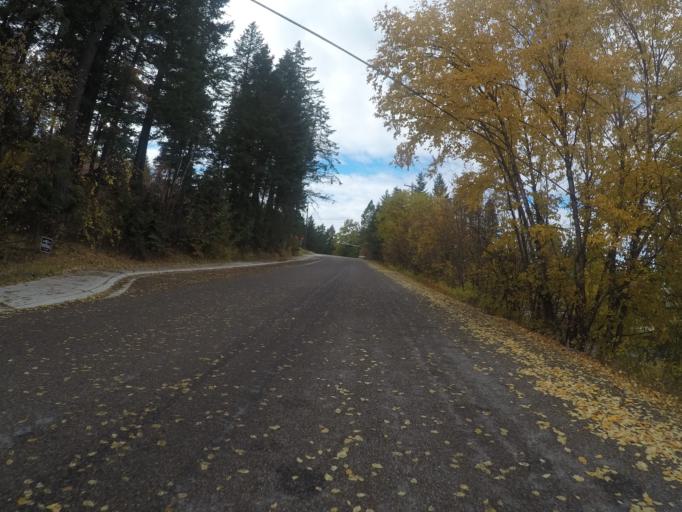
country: US
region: Montana
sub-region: Flathead County
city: Bigfork
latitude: 48.0592
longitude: -114.0756
